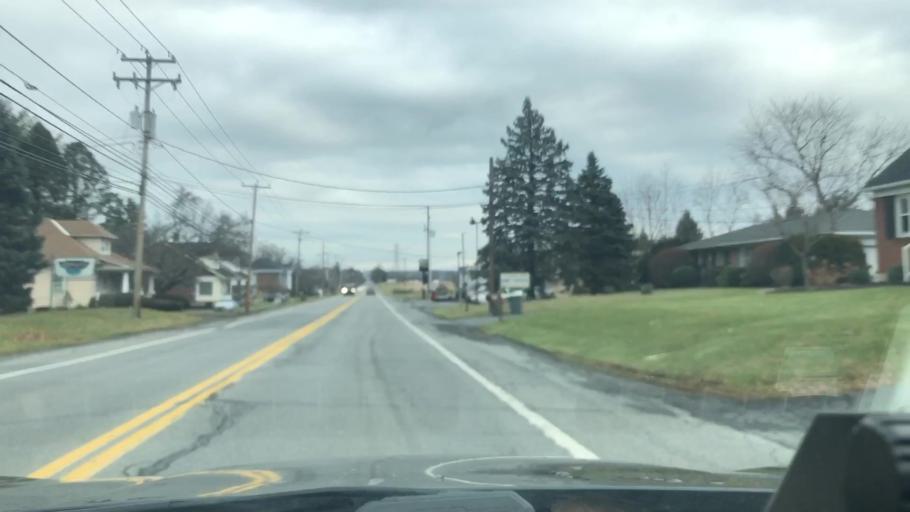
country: US
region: Pennsylvania
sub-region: Northampton County
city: Nazareth
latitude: 40.7141
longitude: -75.3236
